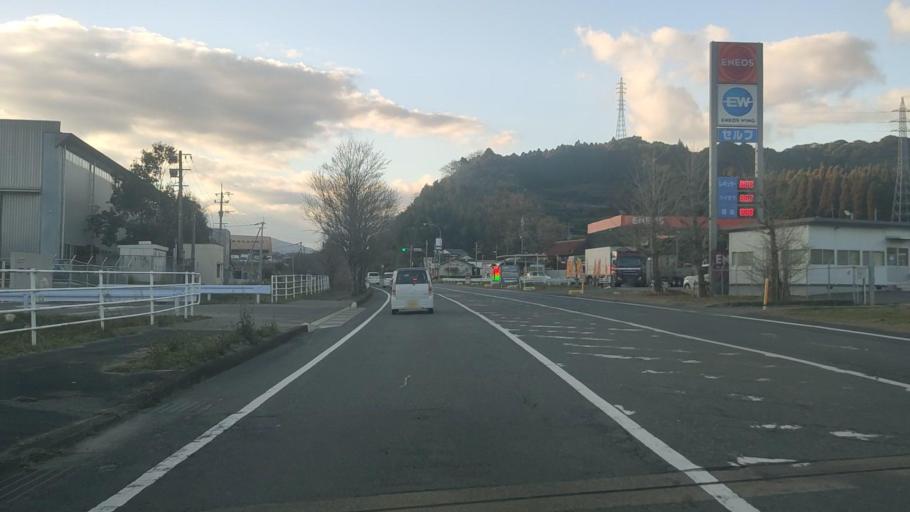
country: JP
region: Saga Prefecture
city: Takeocho-takeo
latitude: 33.2890
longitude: 130.1316
